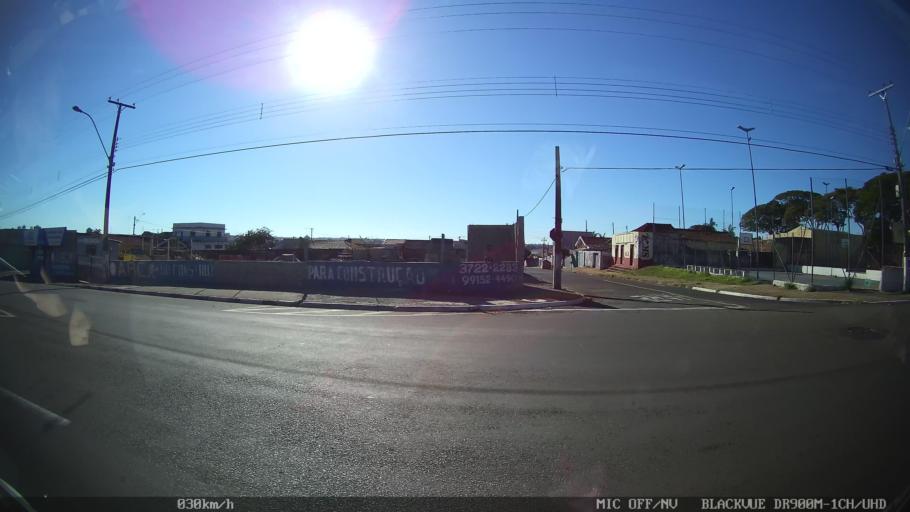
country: BR
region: Sao Paulo
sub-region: Franca
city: Franca
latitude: -20.5603
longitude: -47.3950
